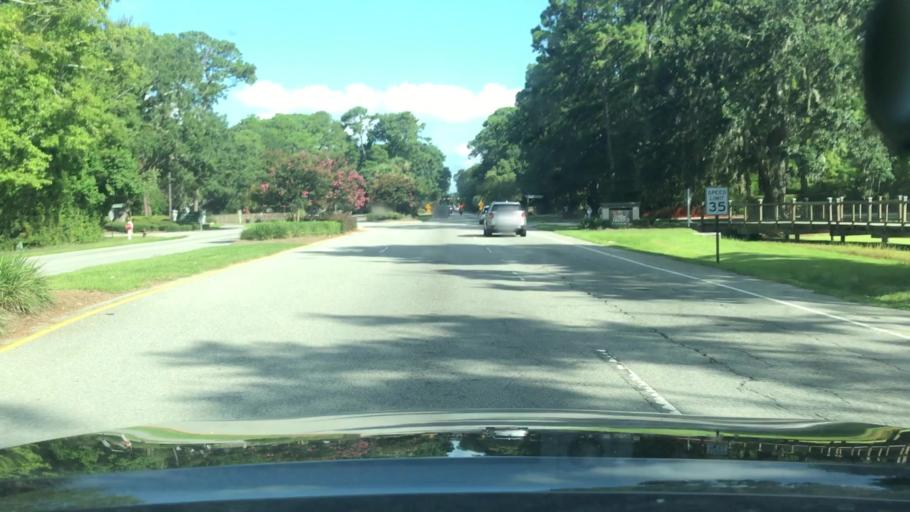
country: US
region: South Carolina
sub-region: Beaufort County
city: Hilton Head Island
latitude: 32.1498
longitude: -80.7578
